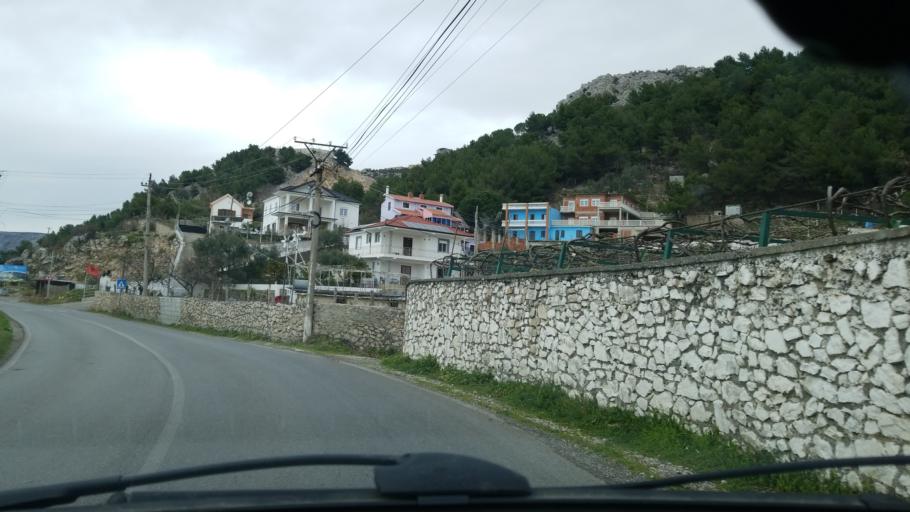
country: AL
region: Lezhe
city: Lezhe
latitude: 41.7873
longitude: 19.6282
